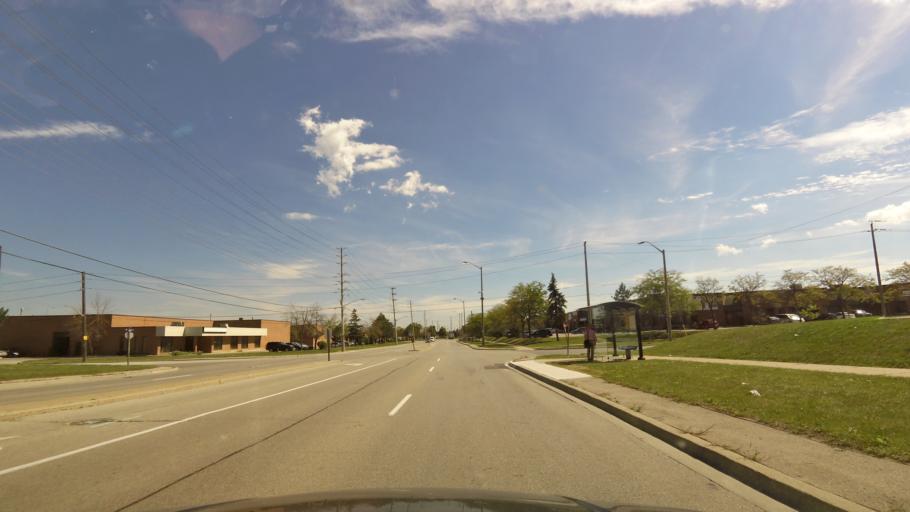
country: CA
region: Ontario
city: Mississauga
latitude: 43.6310
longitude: -79.6383
